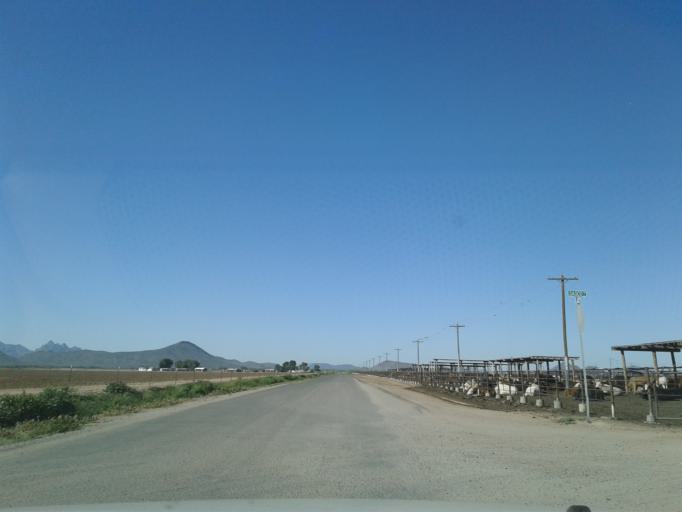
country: US
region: Arizona
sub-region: Pima County
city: Avra Valley
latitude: 32.5571
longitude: -111.3730
